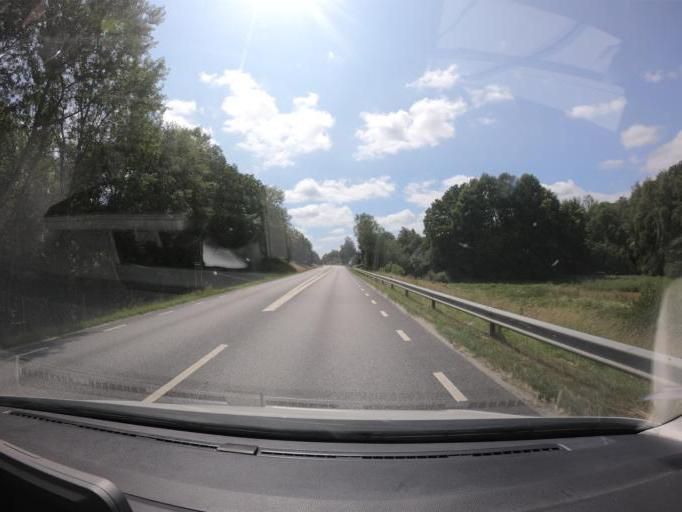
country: SE
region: Skane
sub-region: Hoors Kommun
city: Hoeoer
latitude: 55.9637
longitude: 13.5750
